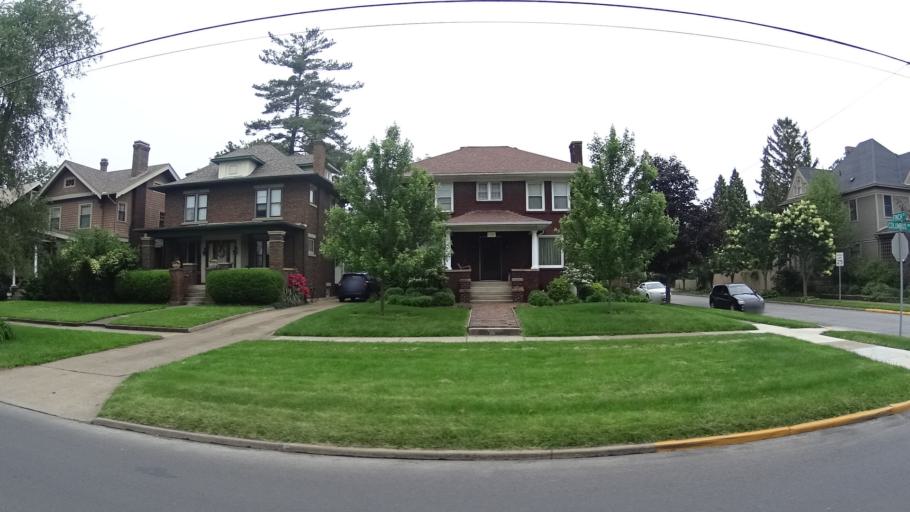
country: US
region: Ohio
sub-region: Erie County
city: Sandusky
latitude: 41.4457
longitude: -82.7056
